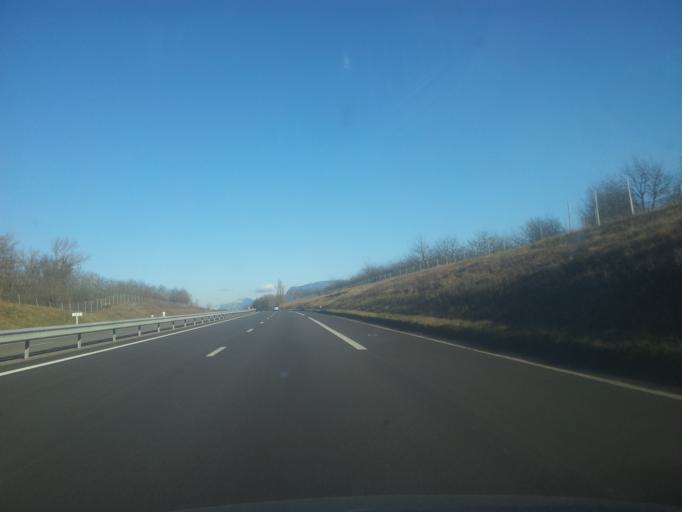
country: FR
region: Rhone-Alpes
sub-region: Departement de l'Isere
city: Saint-Hilaire-du-Rosier
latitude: 45.1158
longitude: 5.2628
